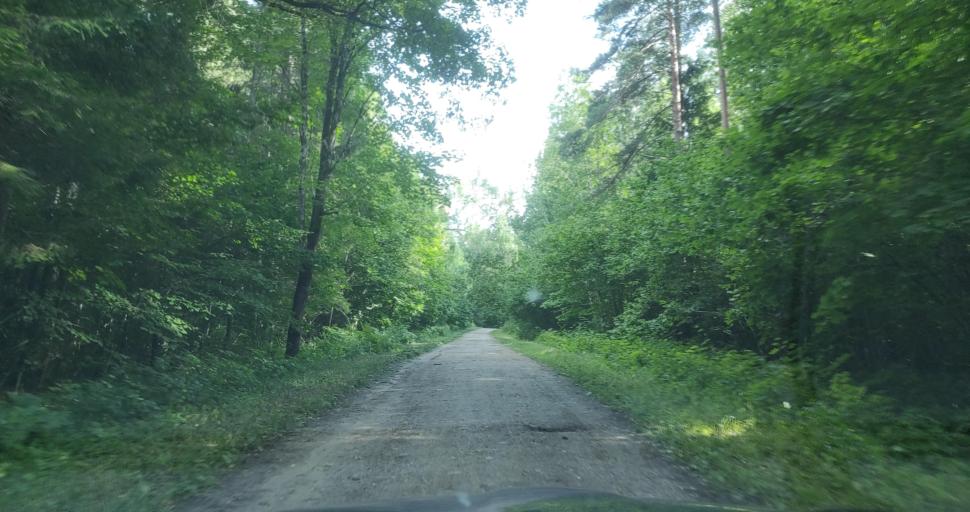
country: LV
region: Kuldigas Rajons
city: Kuldiga
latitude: 56.9925
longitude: 22.0103
